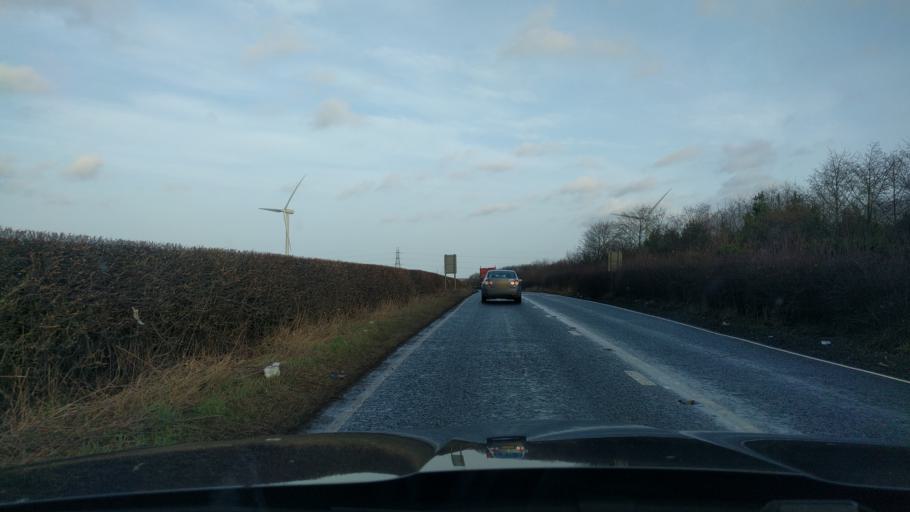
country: GB
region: England
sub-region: Northumberland
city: Cresswell
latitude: 55.1997
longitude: -1.5798
